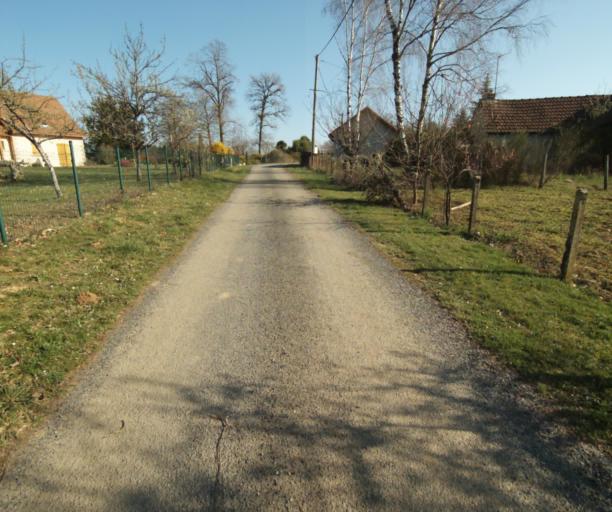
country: FR
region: Limousin
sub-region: Departement de la Correze
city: Saint-Clement
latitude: 45.3201
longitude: 1.6801
